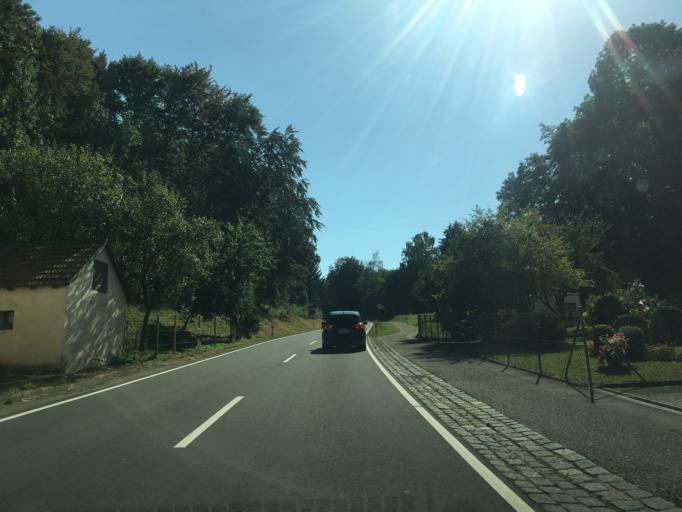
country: DE
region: Baden-Wuerttemberg
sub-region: Tuebingen Region
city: Munsingen
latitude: 48.4003
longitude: 9.4881
